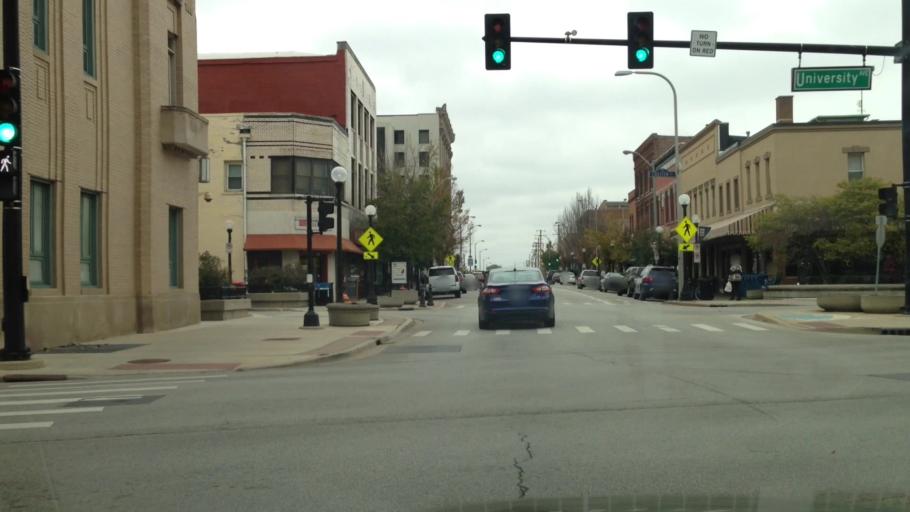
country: US
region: Illinois
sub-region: Champaign County
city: Champaign
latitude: 40.1163
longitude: -88.2427
